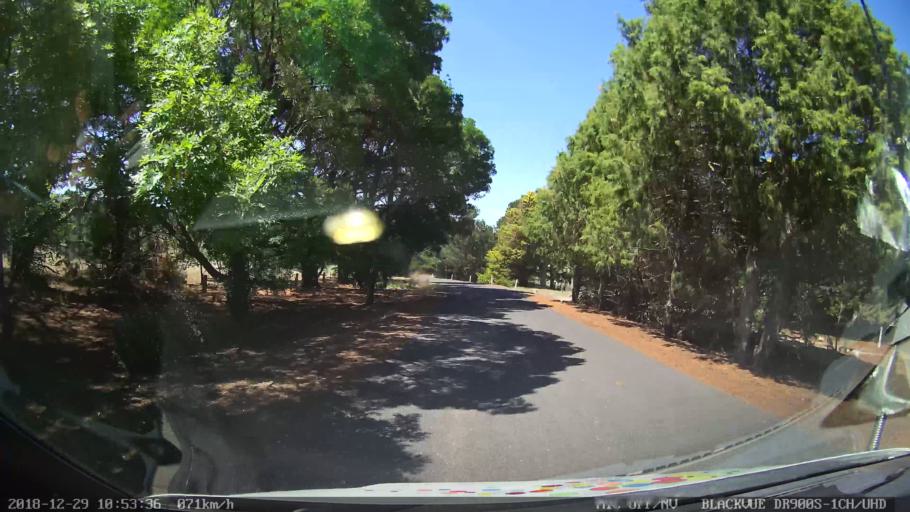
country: AU
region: New South Wales
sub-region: Palerang
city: Bungendore
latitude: -35.1104
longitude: 149.5216
